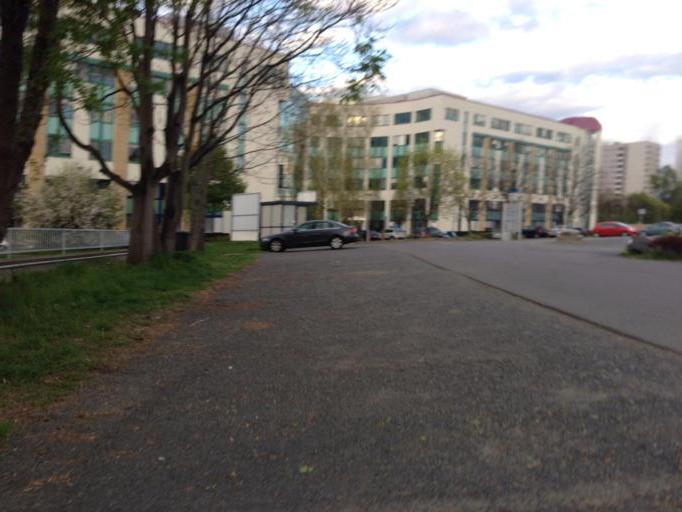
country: DE
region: Saxony
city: Dresden
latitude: 51.0463
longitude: 13.7478
